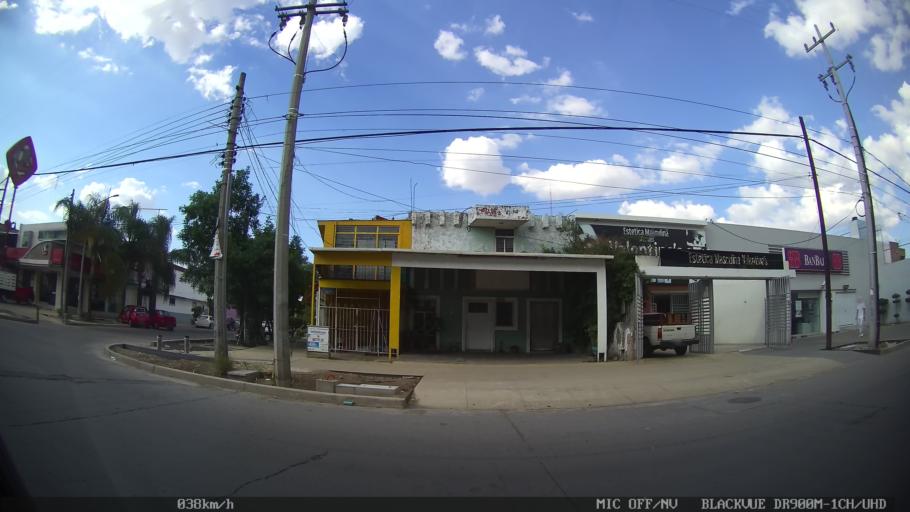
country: MX
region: Jalisco
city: Tlaquepaque
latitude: 20.6528
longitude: -103.3131
